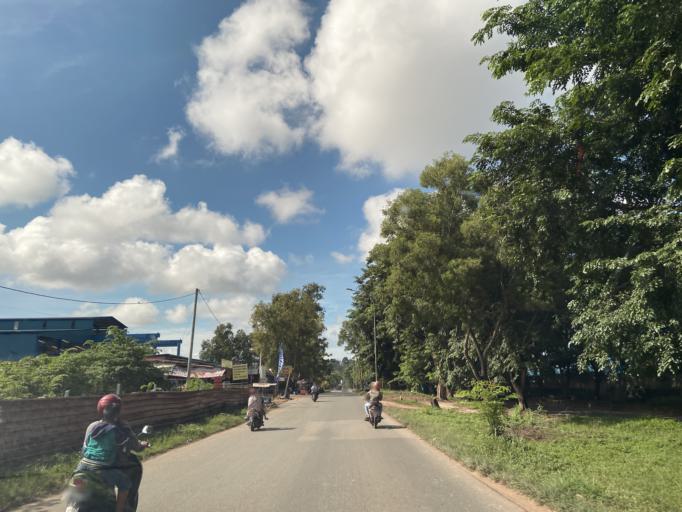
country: SG
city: Singapore
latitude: 1.1687
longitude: 104.0118
